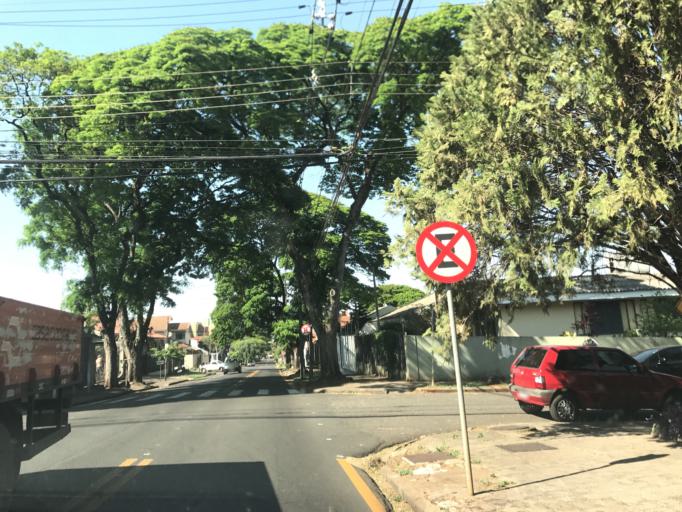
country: BR
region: Parana
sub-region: Maringa
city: Maringa
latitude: -23.4411
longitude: -51.9360
